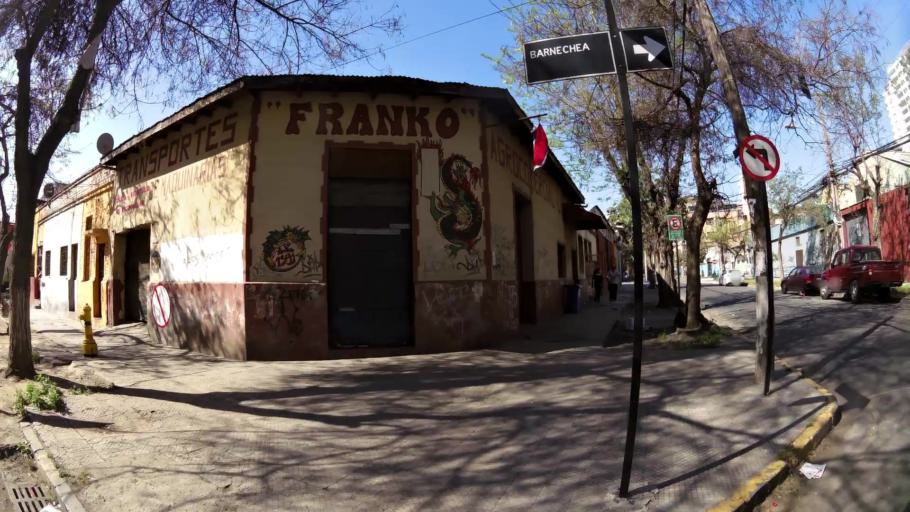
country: CL
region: Santiago Metropolitan
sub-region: Provincia de Santiago
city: Santiago
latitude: -33.4289
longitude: -70.6575
